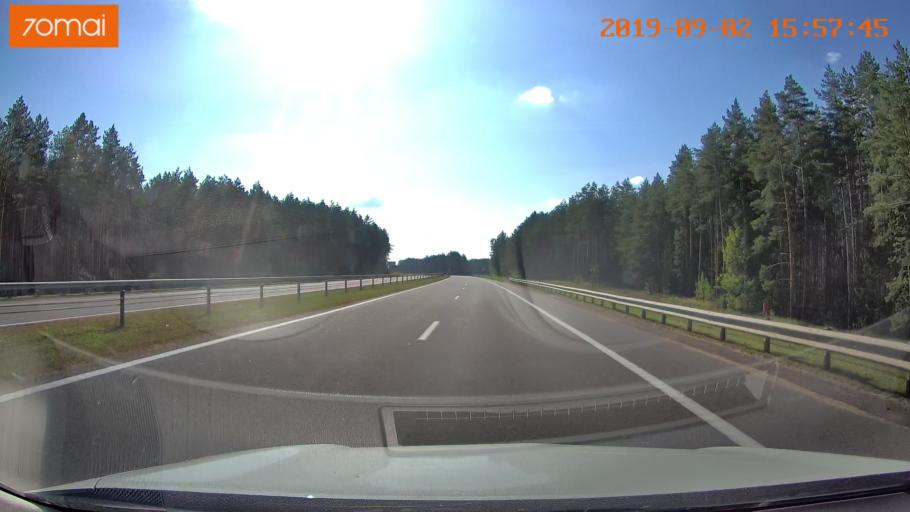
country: BY
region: Minsk
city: Byerazino
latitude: 53.8346
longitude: 29.0312
